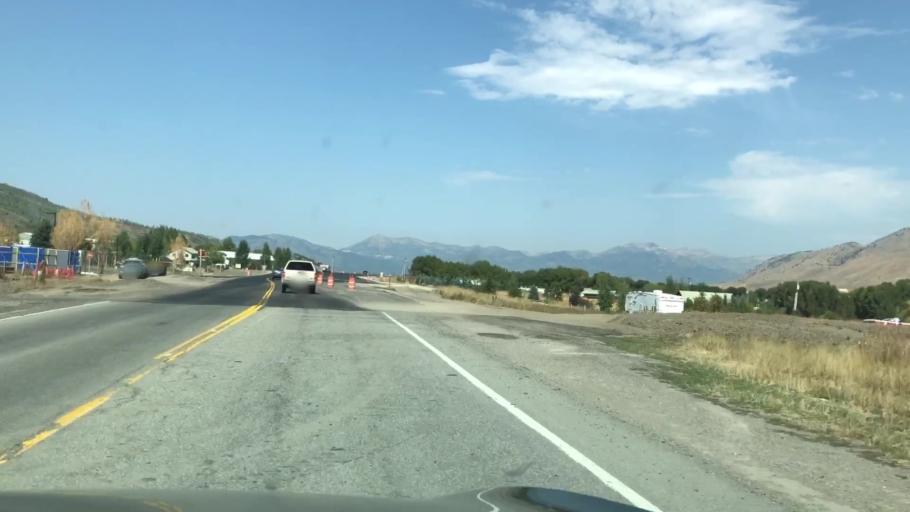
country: US
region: Wyoming
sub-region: Teton County
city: South Park
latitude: 43.3704
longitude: -110.7390
